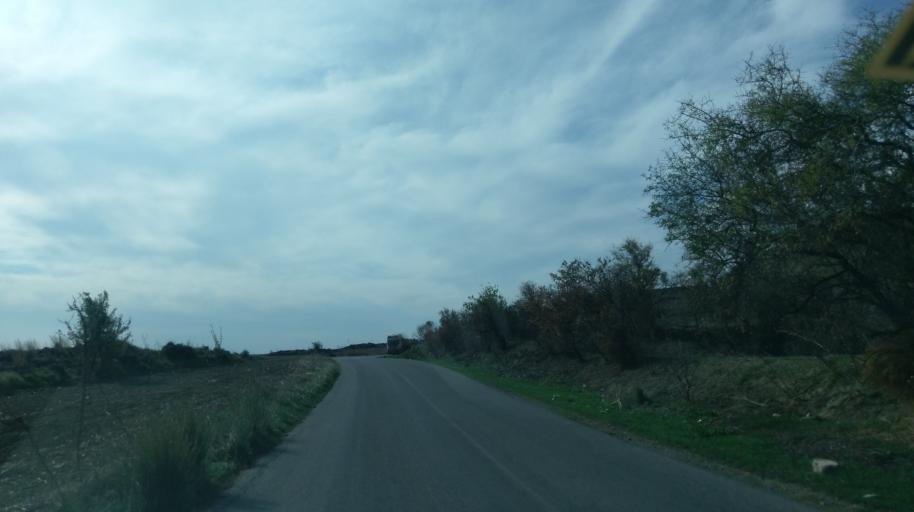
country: CY
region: Keryneia
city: Lapithos
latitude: 35.2806
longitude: 33.2016
